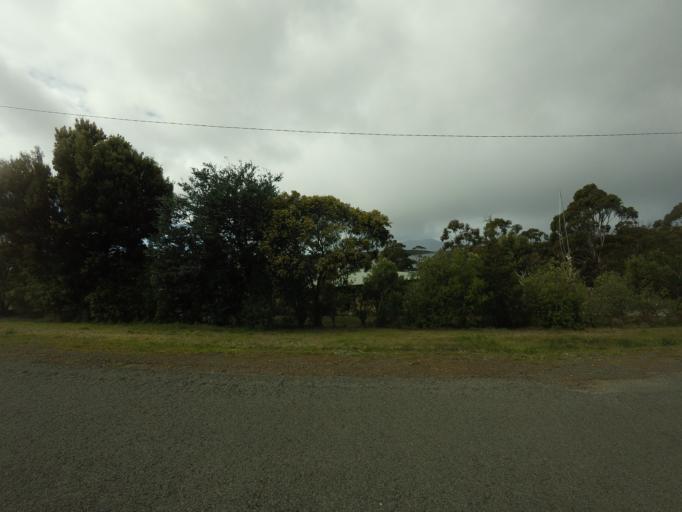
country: AU
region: Tasmania
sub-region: Sorell
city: Sorell
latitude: -42.5408
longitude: 147.9106
